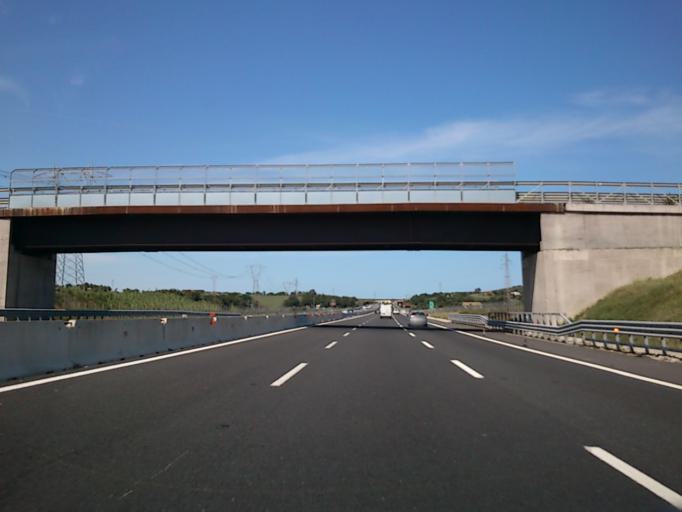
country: IT
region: The Marches
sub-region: Provincia di Pesaro e Urbino
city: Borgo Santa Maria
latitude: 43.9090
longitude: 12.8222
